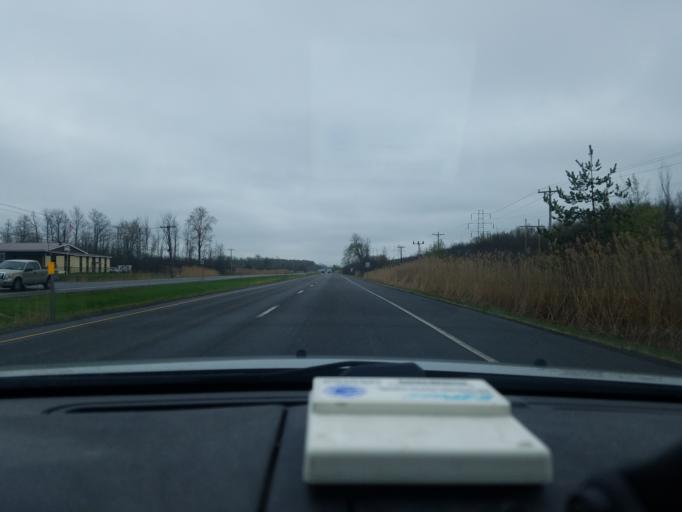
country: US
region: New York
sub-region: Onondaga County
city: North Syracuse
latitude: 43.1221
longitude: -76.0786
